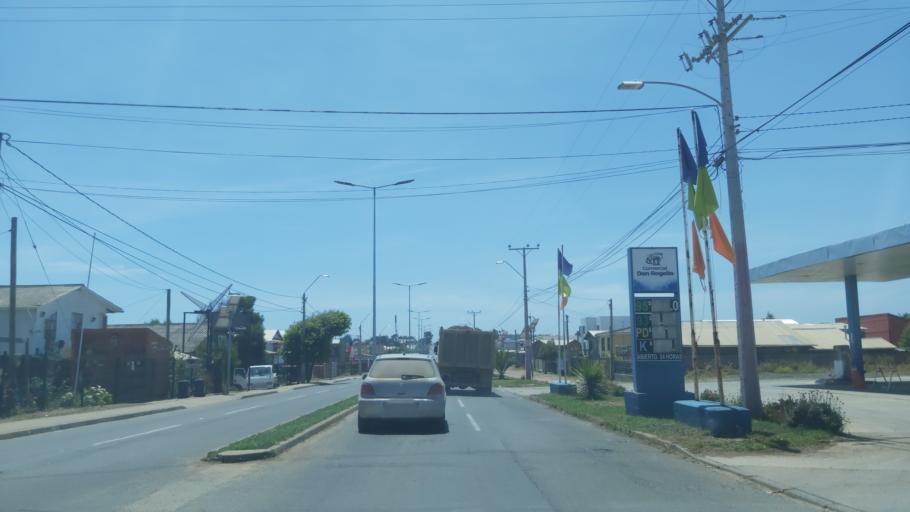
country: CL
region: Maule
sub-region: Provincia de Cauquenes
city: Cauquenes
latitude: -35.8106
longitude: -72.5715
